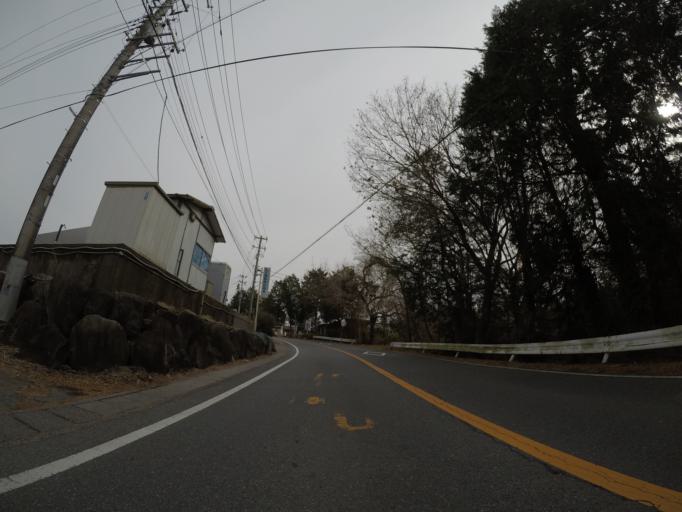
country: JP
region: Shizuoka
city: Fujinomiya
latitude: 35.2151
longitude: 138.6611
